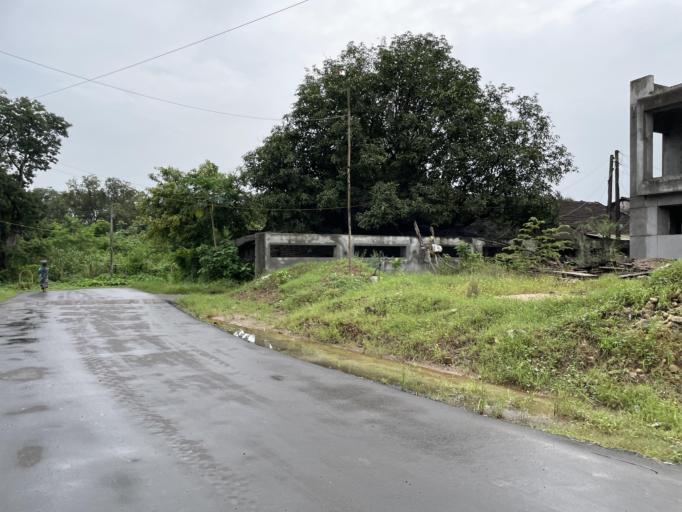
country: IN
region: Gujarat
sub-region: Valsad
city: Pardi
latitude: 20.4539
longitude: 72.9325
